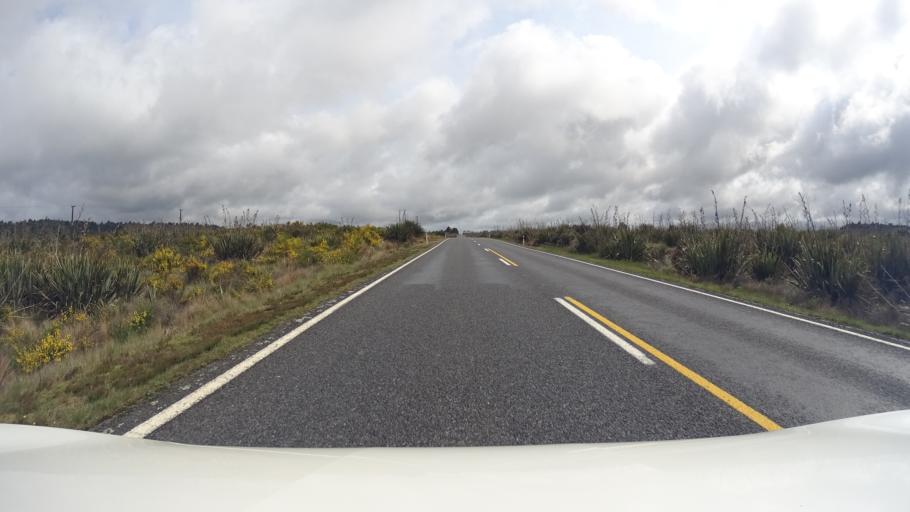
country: NZ
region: Manawatu-Wanganui
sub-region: Ruapehu District
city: Waiouru
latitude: -39.1924
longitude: 175.4015
